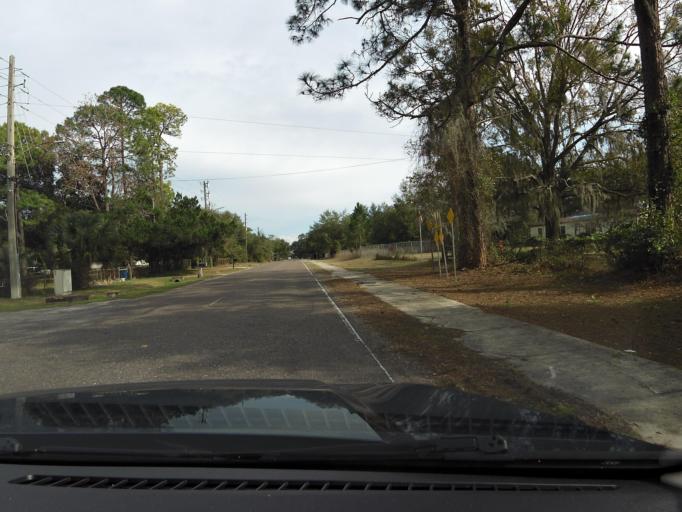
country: US
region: Florida
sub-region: Duval County
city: Jacksonville
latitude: 30.4415
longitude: -81.6016
